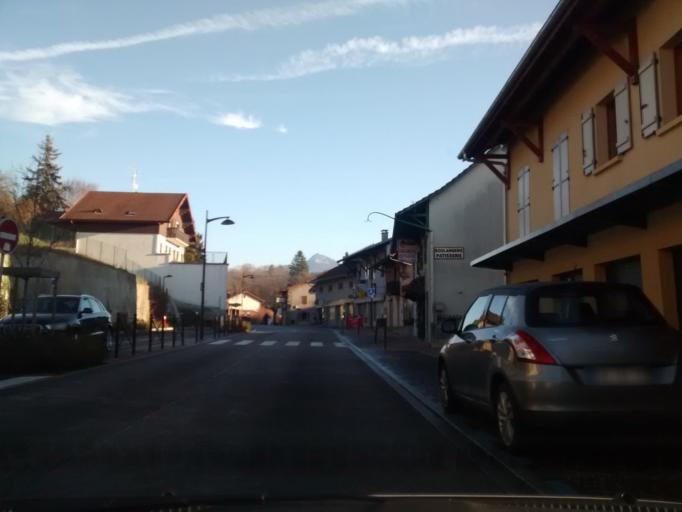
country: FR
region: Rhone-Alpes
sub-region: Departement de la Haute-Savoie
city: Bonne-sur-Menoge
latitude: 46.1670
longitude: 6.3223
